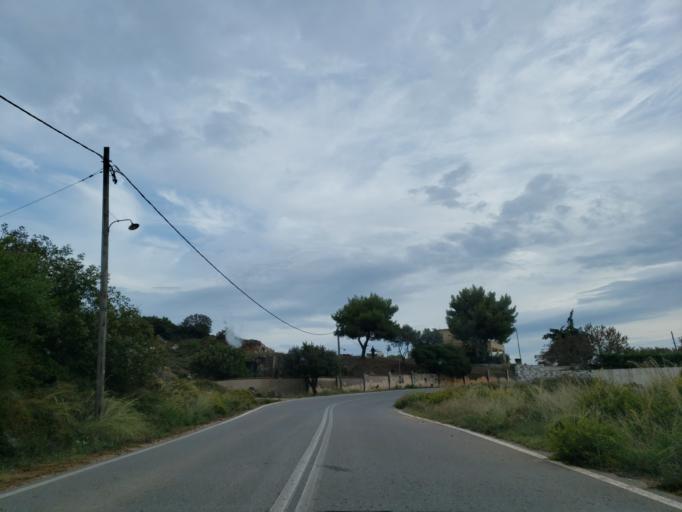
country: GR
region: Attica
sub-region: Nomarchia Anatolikis Attikis
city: Varnavas
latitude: 38.2181
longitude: 23.9399
